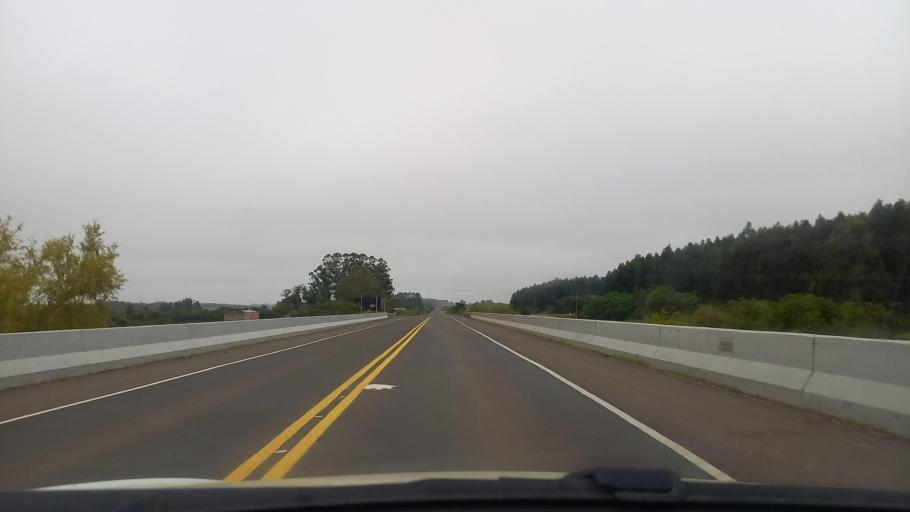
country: BR
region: Rio Grande do Sul
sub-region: Rosario Do Sul
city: Rosario do Sul
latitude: -30.2945
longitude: -54.9880
